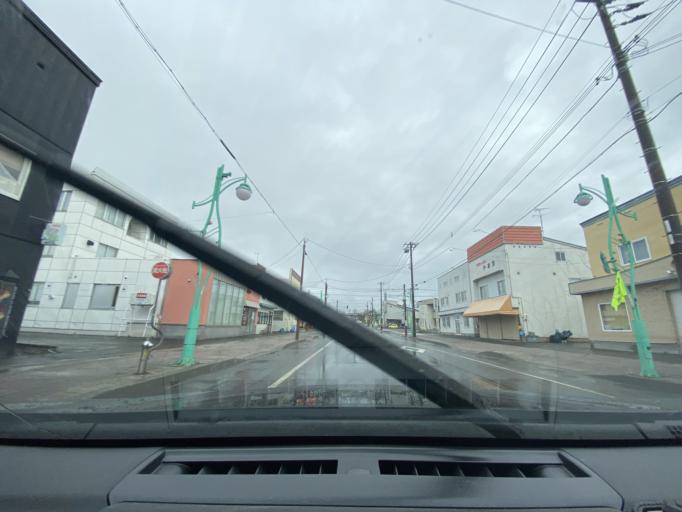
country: JP
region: Hokkaido
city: Fukagawa
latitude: 43.8082
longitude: 141.9346
